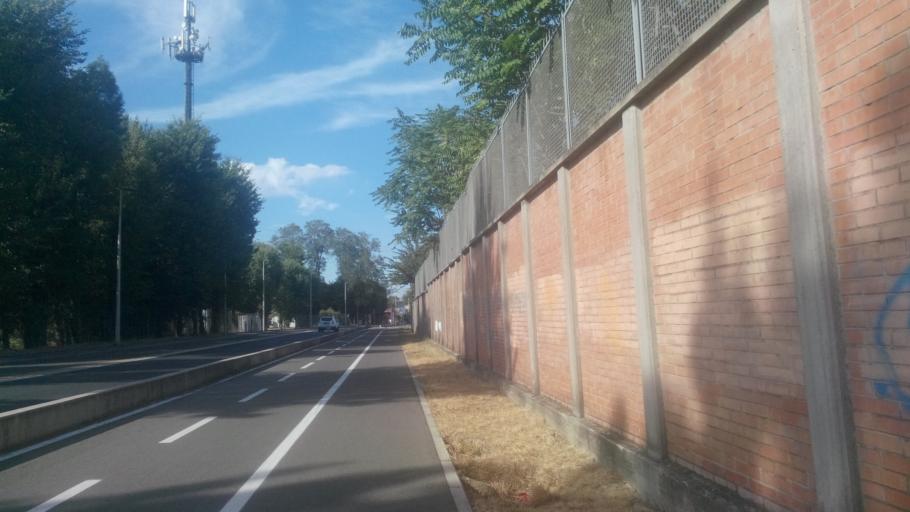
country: IT
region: Emilia-Romagna
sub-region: Provincia di Bologna
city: Bologna
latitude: 44.5215
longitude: 11.3583
